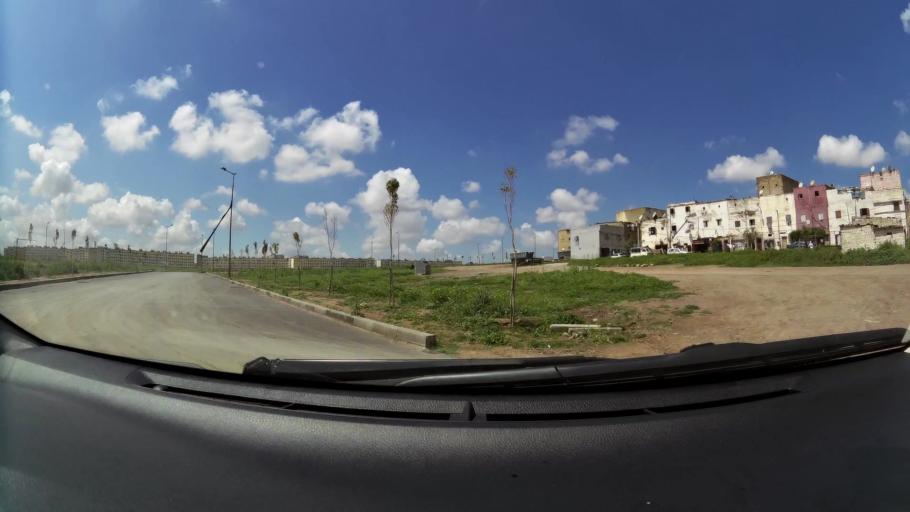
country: MA
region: Grand Casablanca
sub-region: Mediouna
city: Tit Mellil
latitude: 33.5427
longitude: -7.5449
